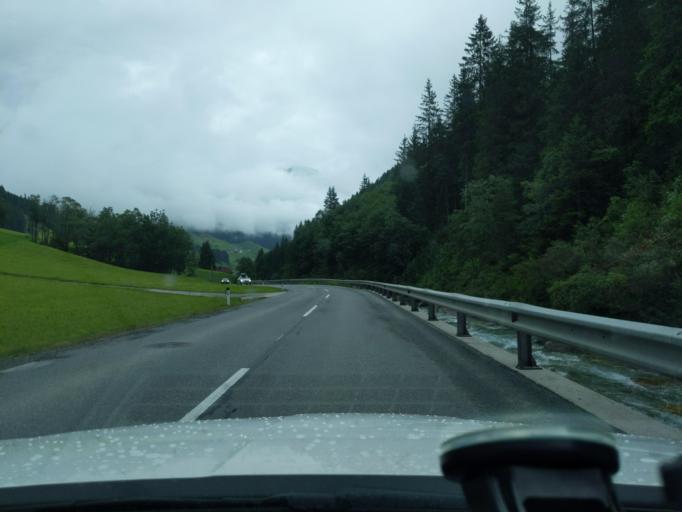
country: AT
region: Tyrol
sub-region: Politischer Bezirk Schwaz
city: Schwendau
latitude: 47.1500
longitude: 11.7218
